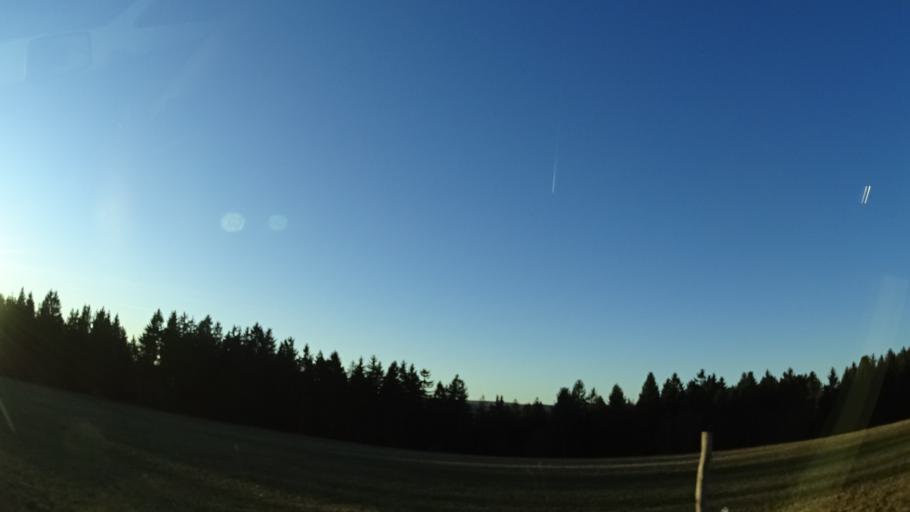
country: DE
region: Thuringia
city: Reichmannsdorf
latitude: 50.5456
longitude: 11.2655
